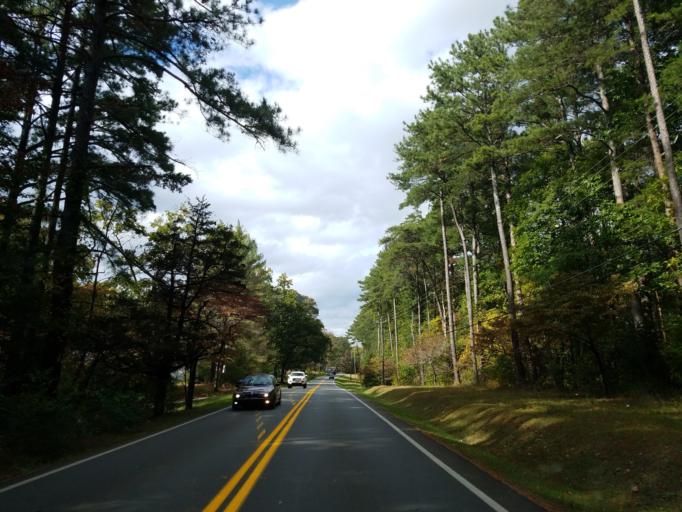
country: US
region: Georgia
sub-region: Pickens County
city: Jasper
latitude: 34.4483
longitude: -84.4228
